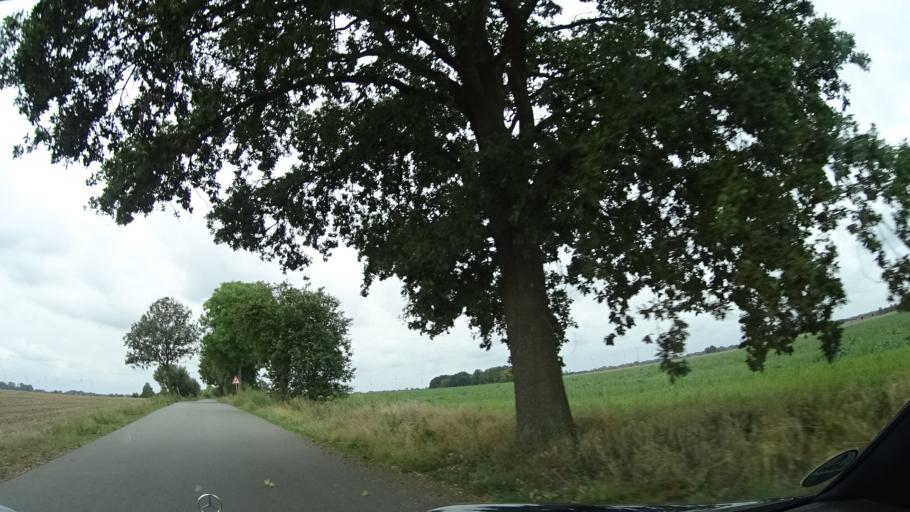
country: DE
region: Brandenburg
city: Neuruppin
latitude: 52.9483
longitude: 12.7573
